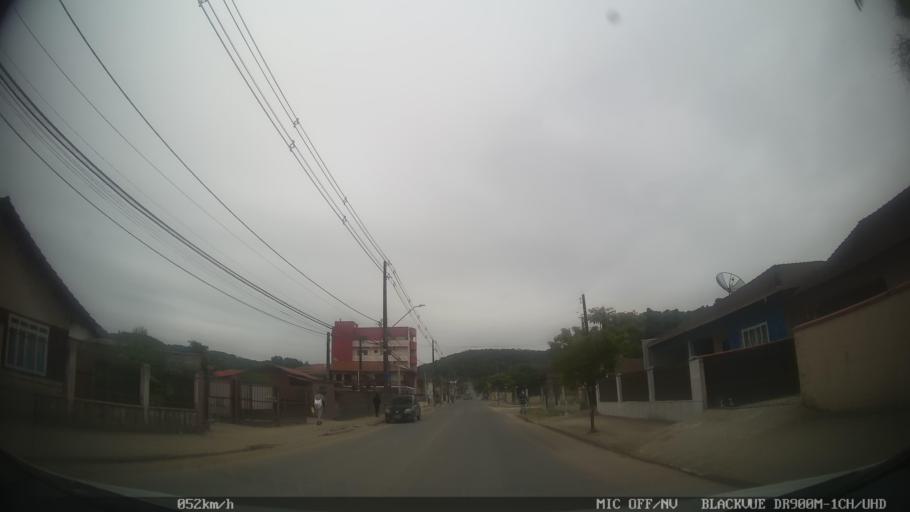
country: BR
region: Santa Catarina
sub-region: Joinville
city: Joinville
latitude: -26.3484
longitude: -48.7934
